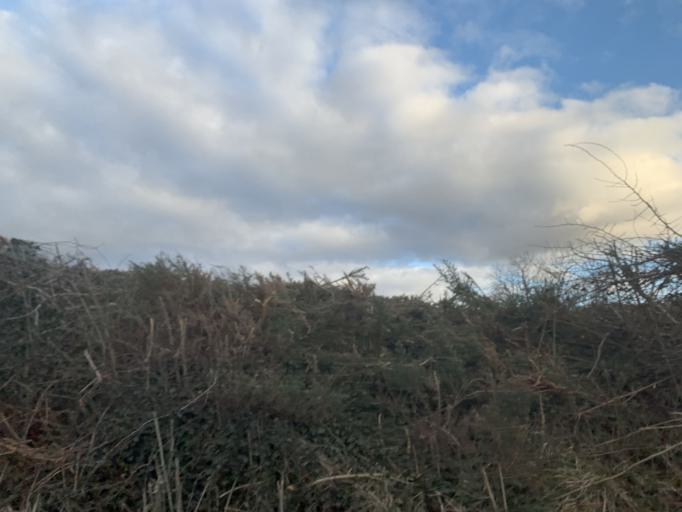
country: IE
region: Connaught
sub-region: Maigh Eo
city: Ballyhaunis
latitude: 53.8535
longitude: -8.7369
